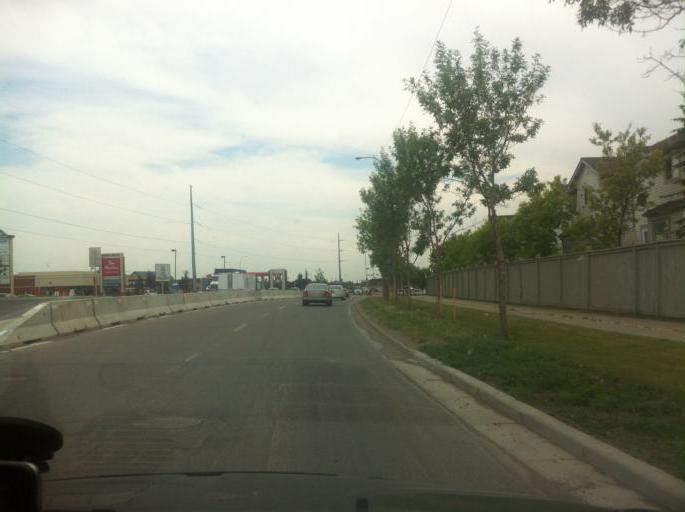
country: CA
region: Alberta
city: Calgary
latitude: 50.9558
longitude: -114.0010
